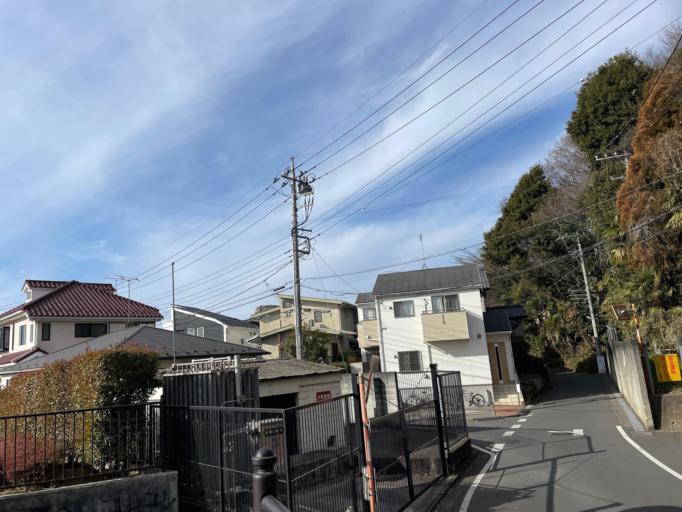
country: JP
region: Saitama
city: Tokorozawa
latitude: 35.7895
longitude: 139.5143
